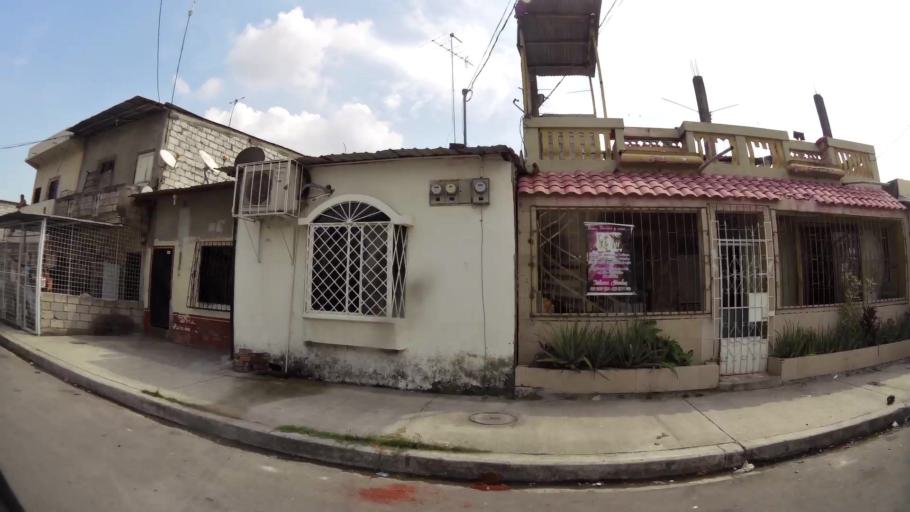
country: EC
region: Guayas
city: Guayaquil
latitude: -2.2840
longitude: -79.8851
